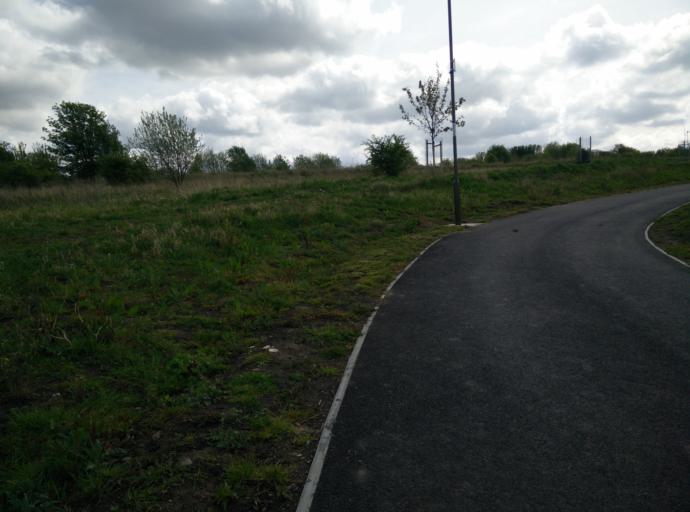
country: GB
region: Scotland
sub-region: Midlothian
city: Bonnyrigg
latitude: 55.9218
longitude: -3.1216
